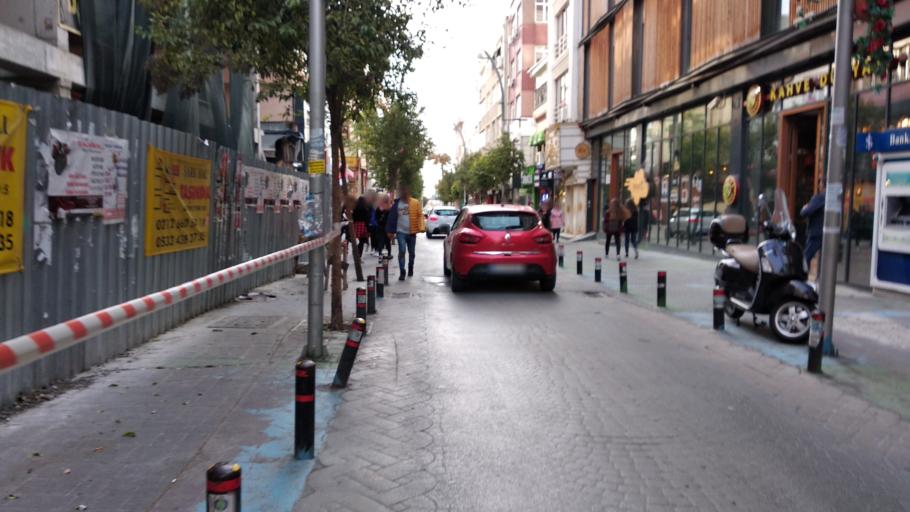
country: TR
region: Istanbul
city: Bahcelievler
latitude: 40.9757
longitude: 28.8752
